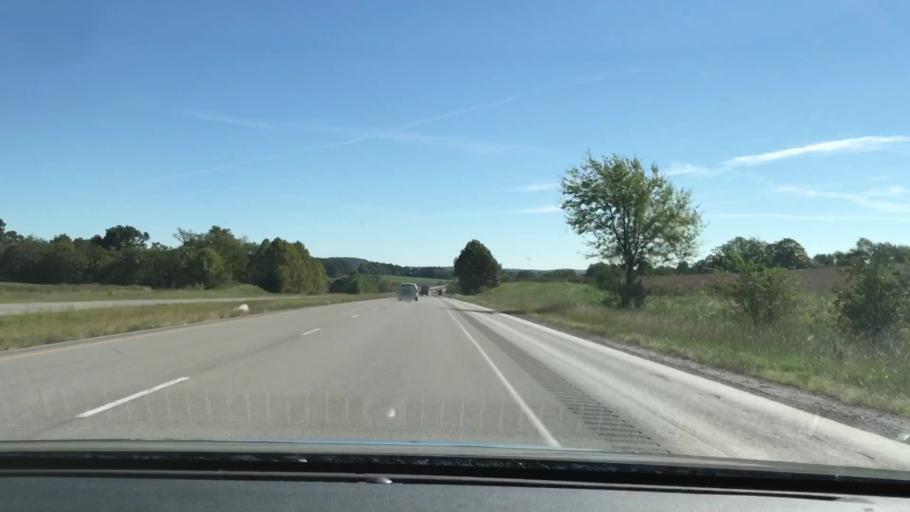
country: US
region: Kentucky
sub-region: Todd County
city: Elkton
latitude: 36.8469
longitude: -87.3093
